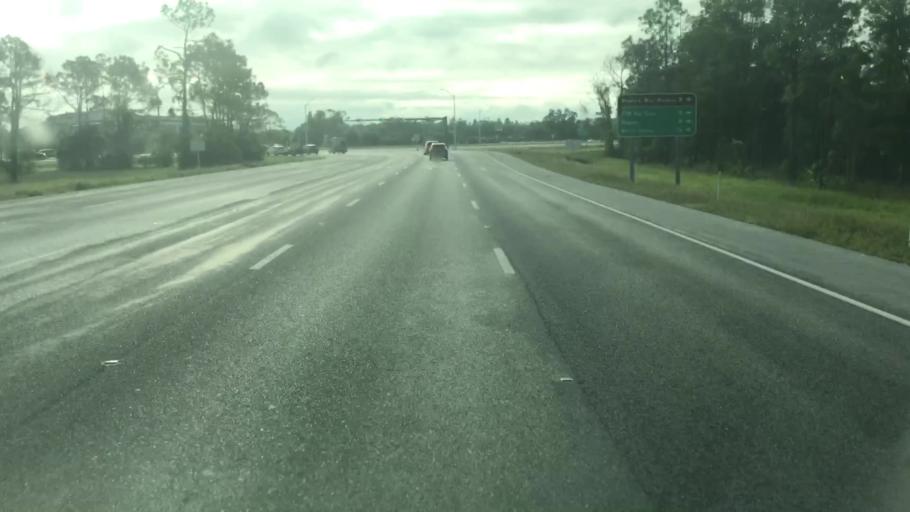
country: US
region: Florida
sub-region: Collier County
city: Golden Gate
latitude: 26.1593
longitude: -81.6882
